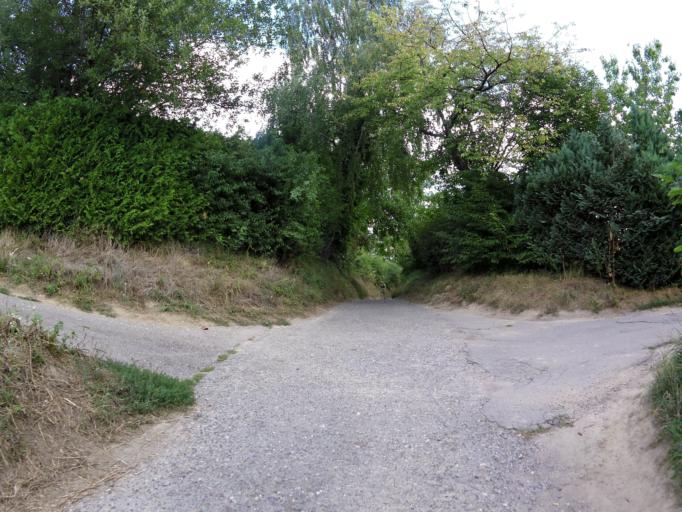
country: DE
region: Baden-Wuerttemberg
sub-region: Freiburg Region
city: Lahr
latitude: 48.3281
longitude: 7.8676
